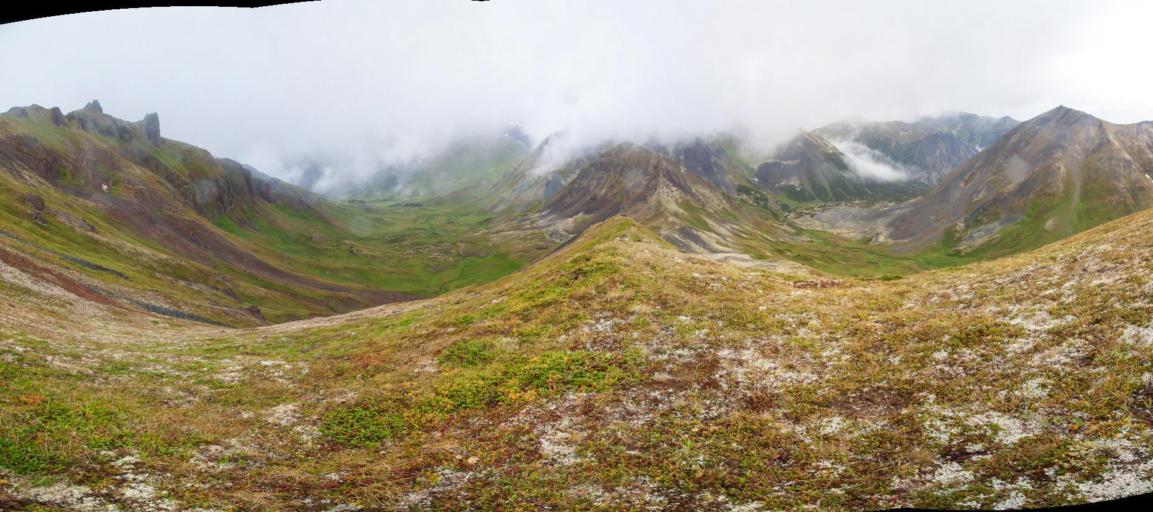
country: RU
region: Kamtsjatka
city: Yelizovo
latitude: 54.0099
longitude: 158.0885
